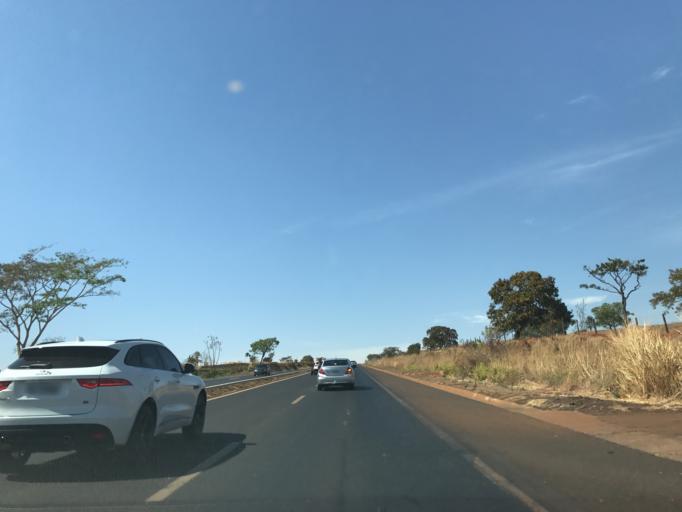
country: BR
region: Minas Gerais
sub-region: Centralina
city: Centralina
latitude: -18.6630
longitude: -49.1656
